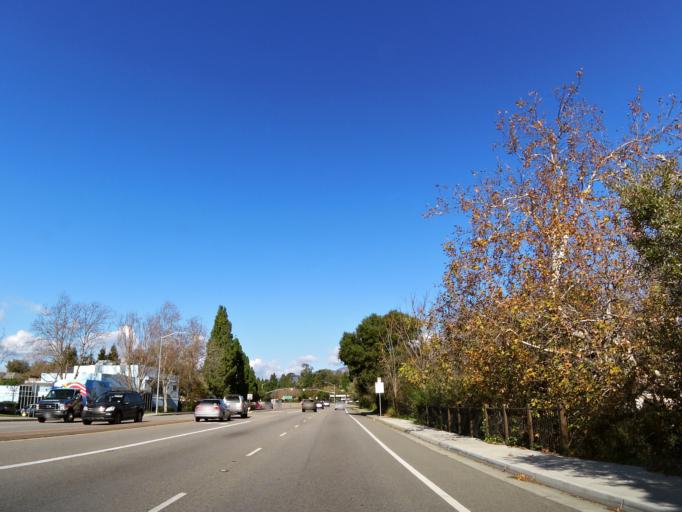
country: US
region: California
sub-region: San Luis Obispo County
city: San Luis Obispo
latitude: 35.2920
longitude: -120.6672
